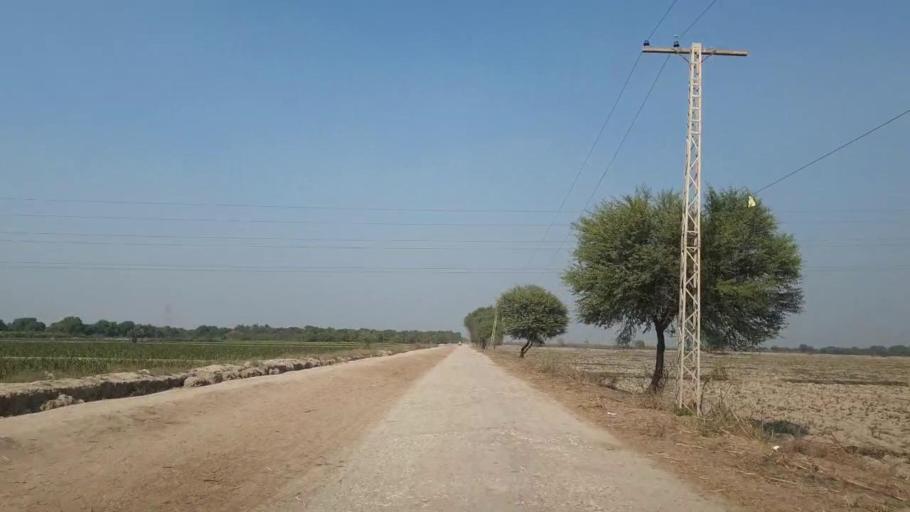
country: PK
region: Sindh
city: Tando Allahyar
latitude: 25.4969
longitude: 68.8221
